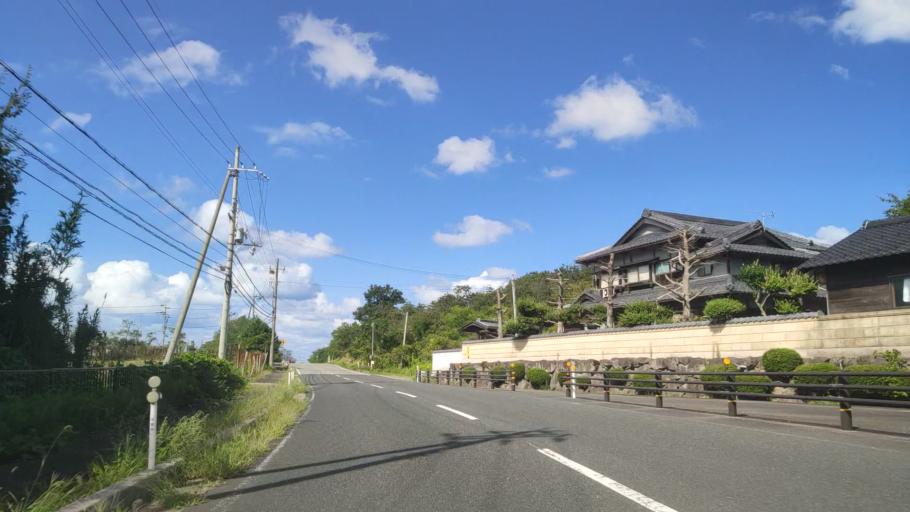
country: JP
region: Hyogo
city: Toyooka
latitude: 35.6472
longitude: 134.9510
